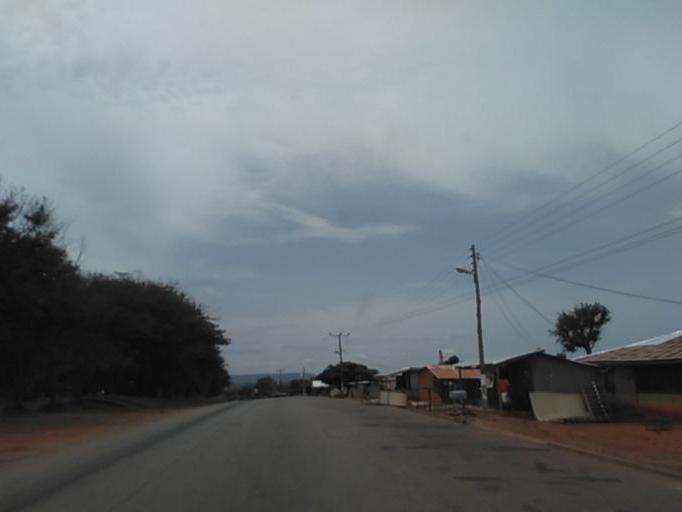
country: GH
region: Ashanti
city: Mampong
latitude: 7.1905
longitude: -1.3985
